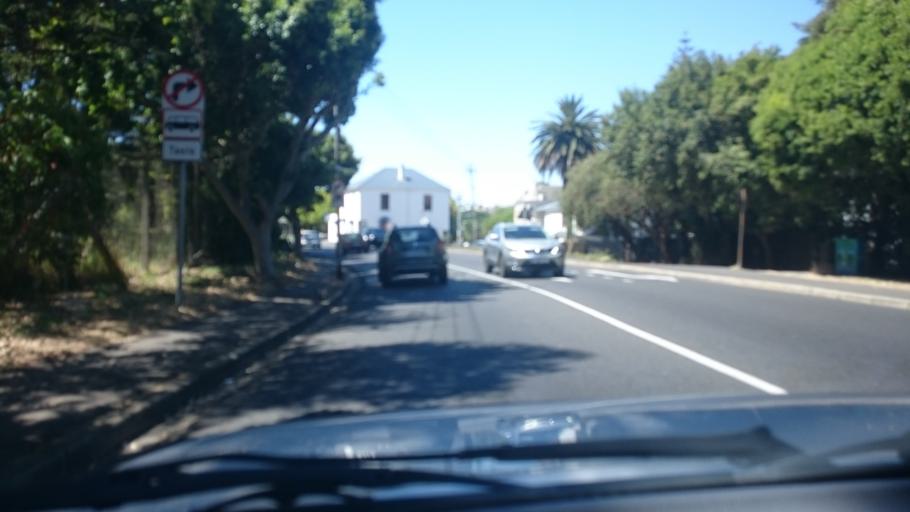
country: ZA
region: Western Cape
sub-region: City of Cape Town
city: Claremont
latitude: -34.0097
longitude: 18.4618
